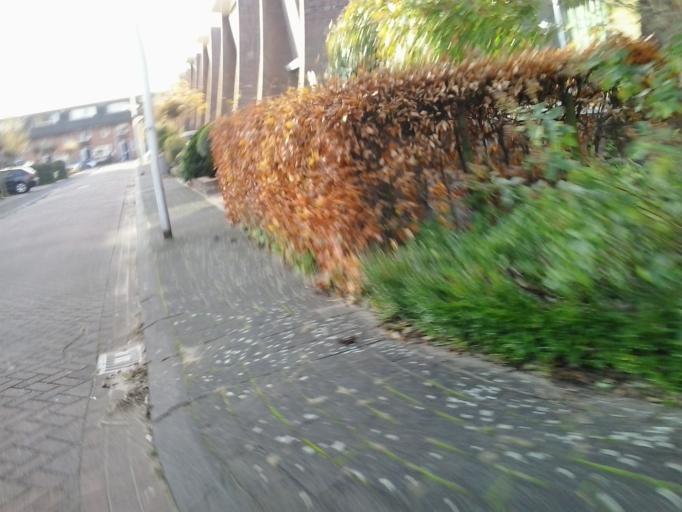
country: NL
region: South Holland
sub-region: Gemeente Lansingerland
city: Bergschenhoek
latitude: 51.9858
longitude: 4.4965
